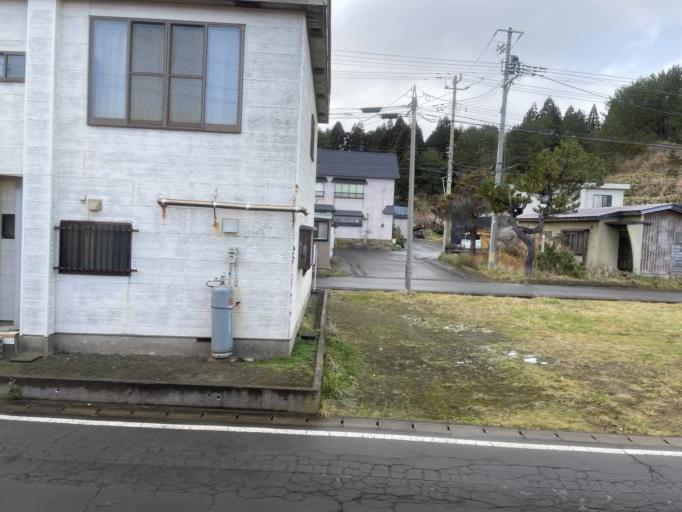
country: JP
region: Aomori
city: Aomori Shi
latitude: 41.0341
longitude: 140.6458
